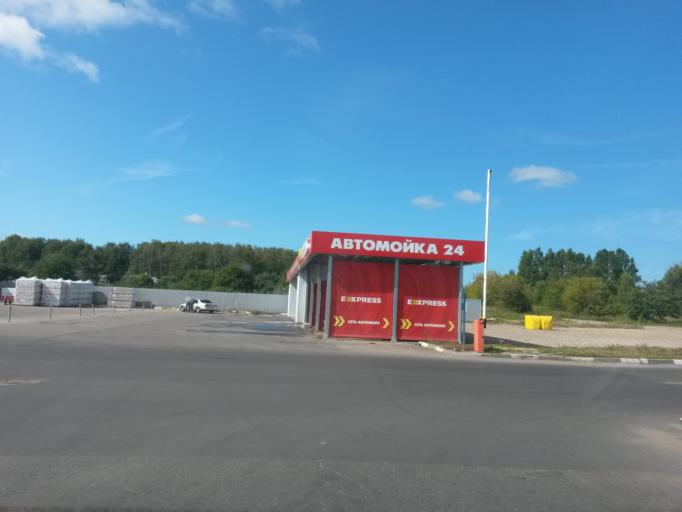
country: RU
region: Jaroslavl
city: Yaroslavl
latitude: 57.5917
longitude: 39.8950
